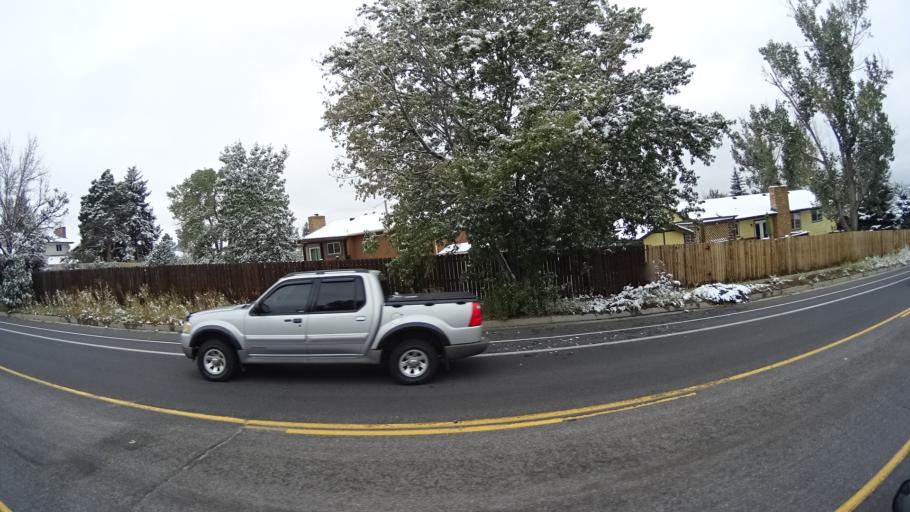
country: US
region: Colorado
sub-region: El Paso County
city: Cimarron Hills
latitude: 38.9223
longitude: -104.7670
